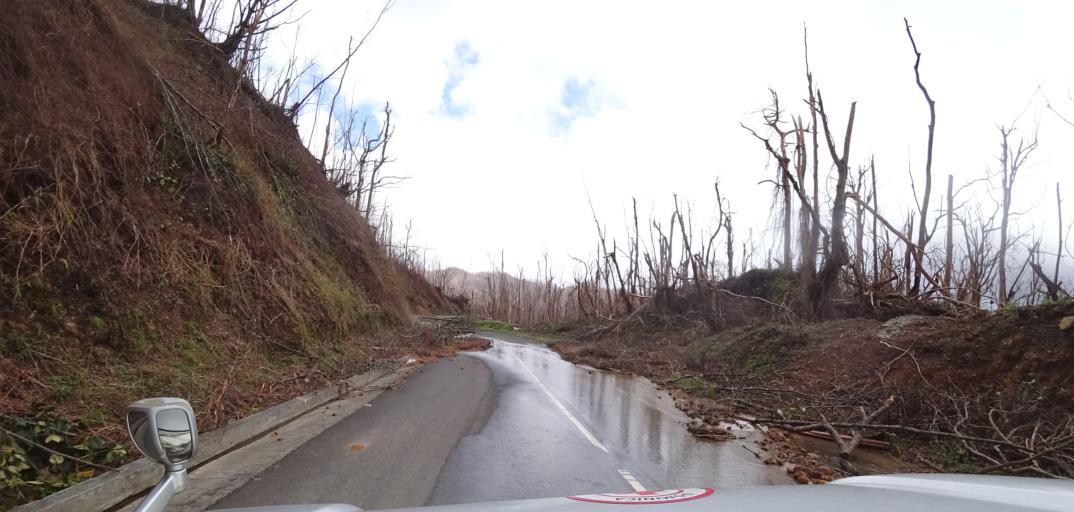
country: DM
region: Saint David
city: Castle Bruce
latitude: 15.4608
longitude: -61.3152
